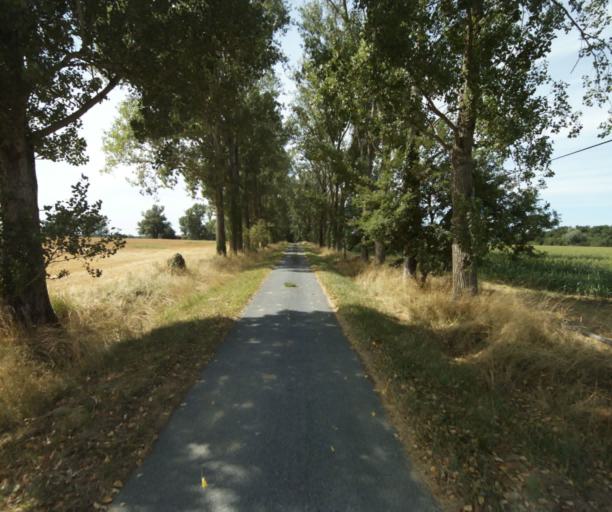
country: FR
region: Midi-Pyrenees
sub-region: Departement du Tarn
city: Soreze
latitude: 43.5061
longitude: 2.0522
